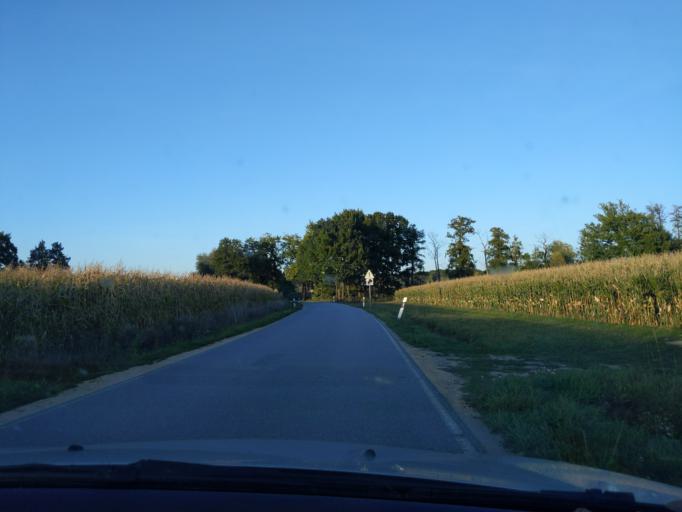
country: DE
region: Saxony
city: Guttau
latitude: 51.2659
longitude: 14.5662
